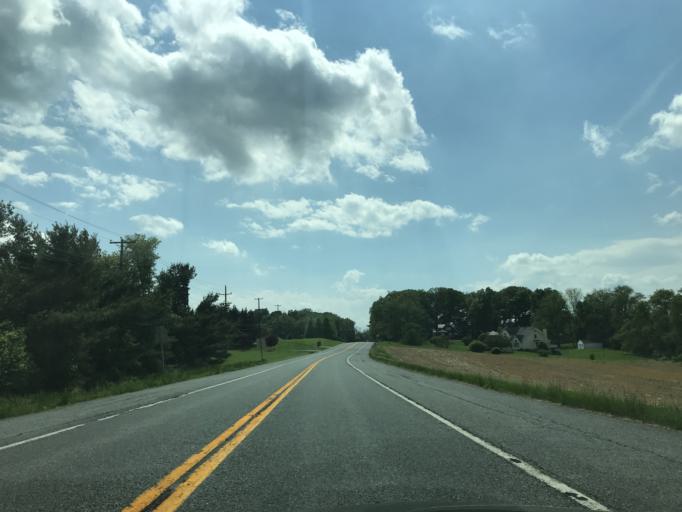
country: US
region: Pennsylvania
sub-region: York County
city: Susquehanna Trails
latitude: 39.6790
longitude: -76.3909
